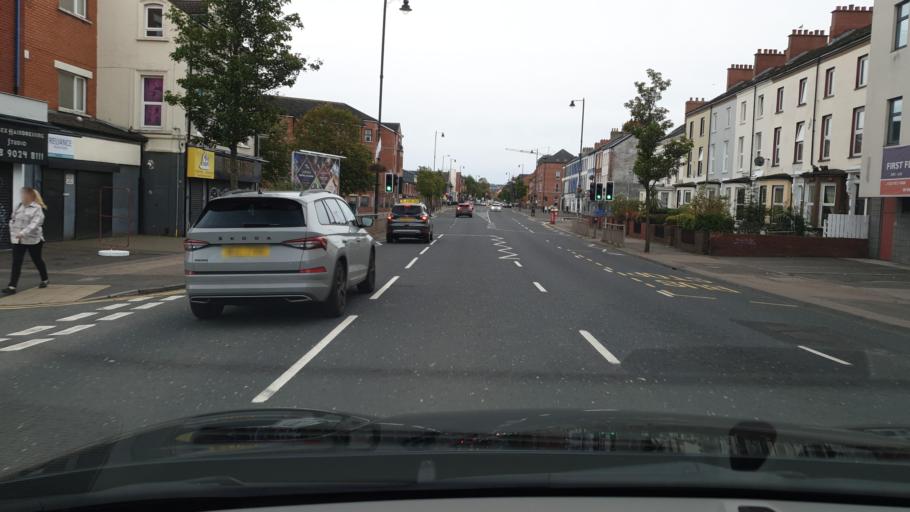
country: GB
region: Northern Ireland
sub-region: City of Belfast
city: Belfast
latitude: 54.5880
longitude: -5.9241
